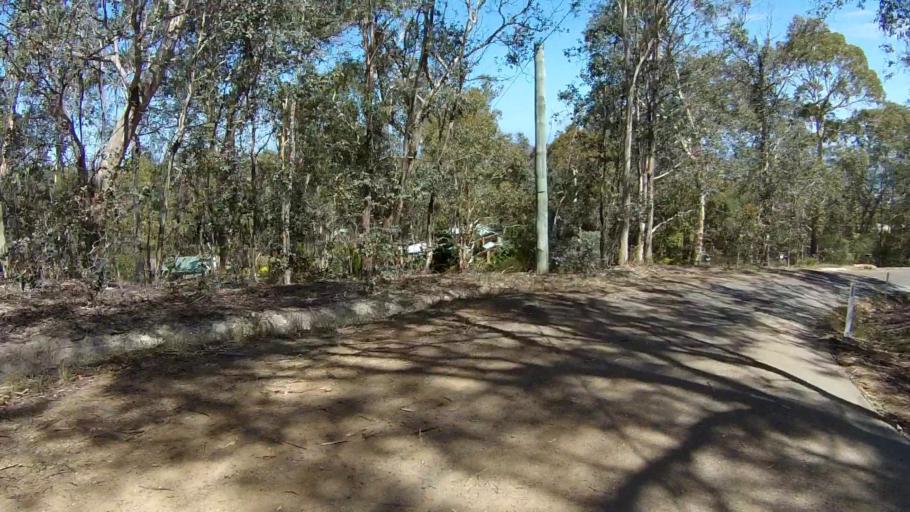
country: AU
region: Tasmania
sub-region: Clarence
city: Sandford
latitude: -42.9746
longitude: 147.4856
